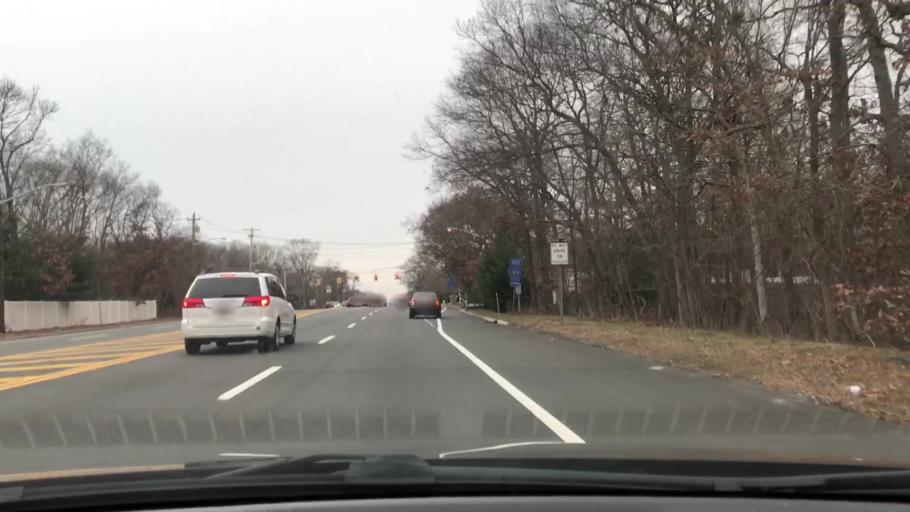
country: US
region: New York
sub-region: Suffolk County
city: North Patchogue
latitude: 40.7921
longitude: -73.0169
